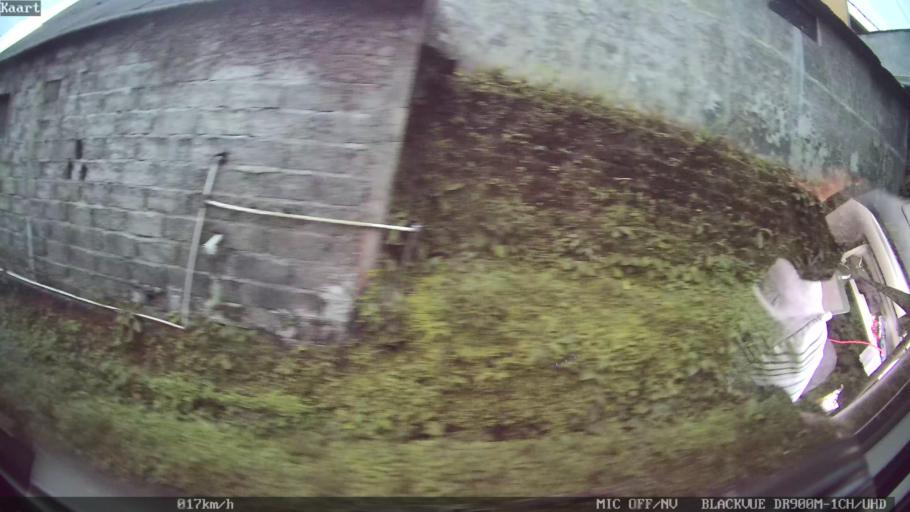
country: ID
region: Bali
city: Peneng
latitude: -8.3518
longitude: 115.2075
